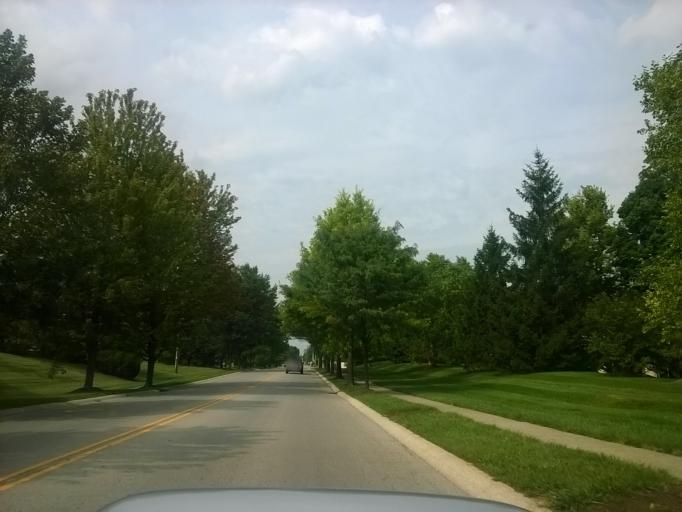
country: US
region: Indiana
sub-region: Hamilton County
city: Carmel
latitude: 39.9697
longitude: -86.1410
